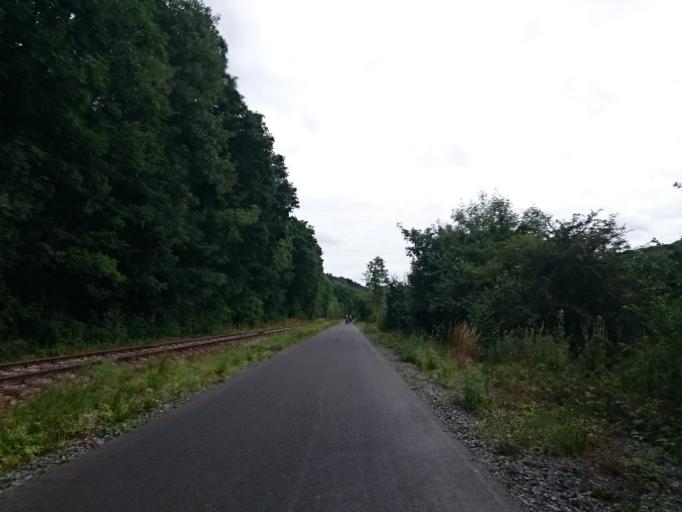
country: FR
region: Lower Normandy
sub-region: Departement du Calvados
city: Clinchamps-sur-Orne
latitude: 49.0754
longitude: -0.4292
